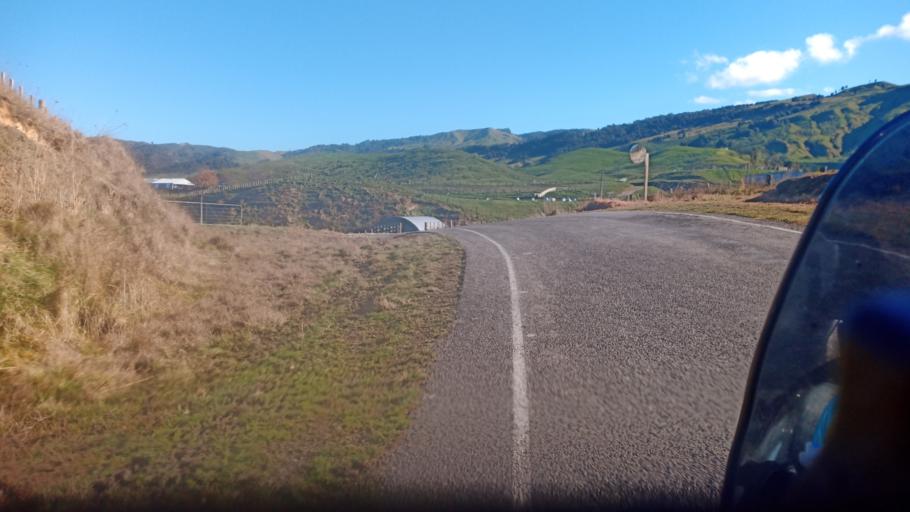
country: NZ
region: Gisborne
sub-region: Gisborne District
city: Gisborne
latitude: -38.5796
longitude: 177.5551
